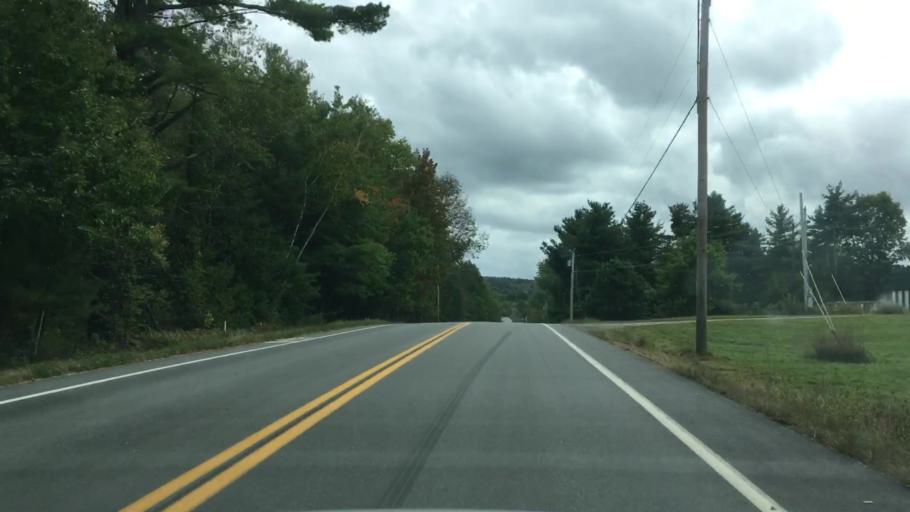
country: US
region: Maine
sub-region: Penobscot County
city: Hermon
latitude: 44.7534
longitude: -68.9717
